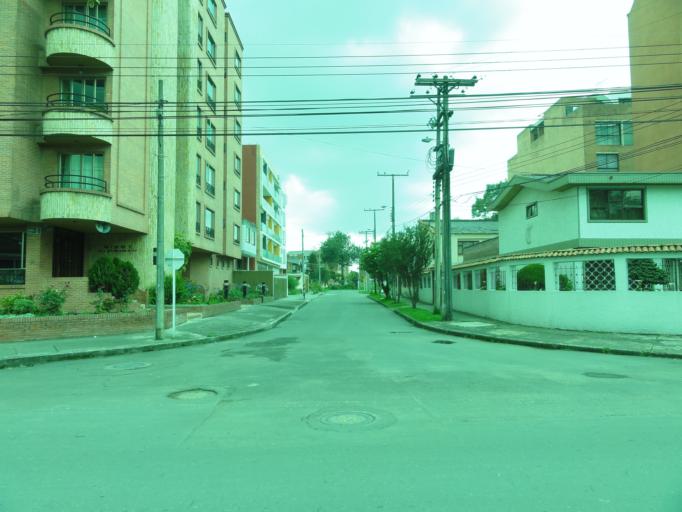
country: CO
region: Bogota D.C.
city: Bogota
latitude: 4.6512
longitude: -74.0829
